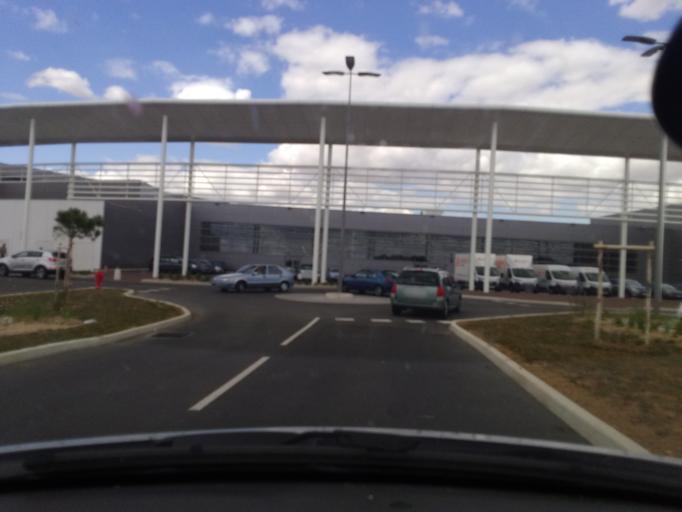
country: FR
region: Centre
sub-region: Departement d'Eure-et-Loir
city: Barjouville
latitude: 48.4099
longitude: 1.4645
